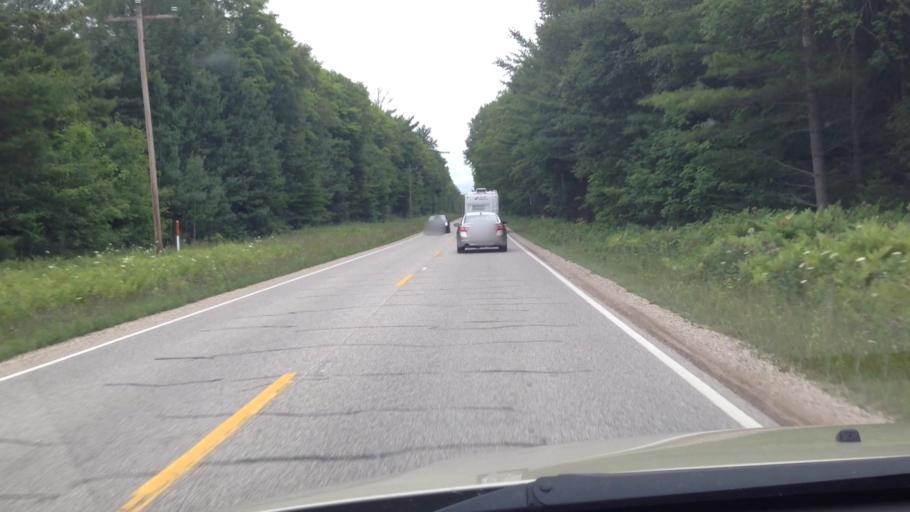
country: US
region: Michigan
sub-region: Mackinac County
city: Saint Ignace
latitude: 46.0568
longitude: -85.1480
